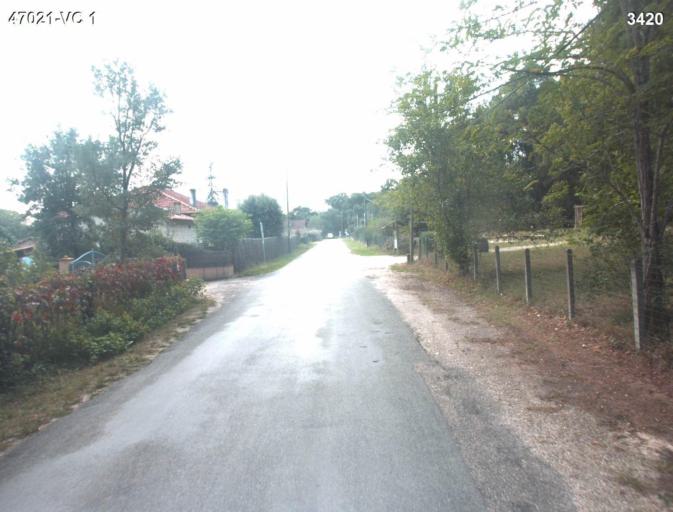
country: FR
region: Aquitaine
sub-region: Departement du Lot-et-Garonne
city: Barbaste
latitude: 44.1379
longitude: 0.2910
